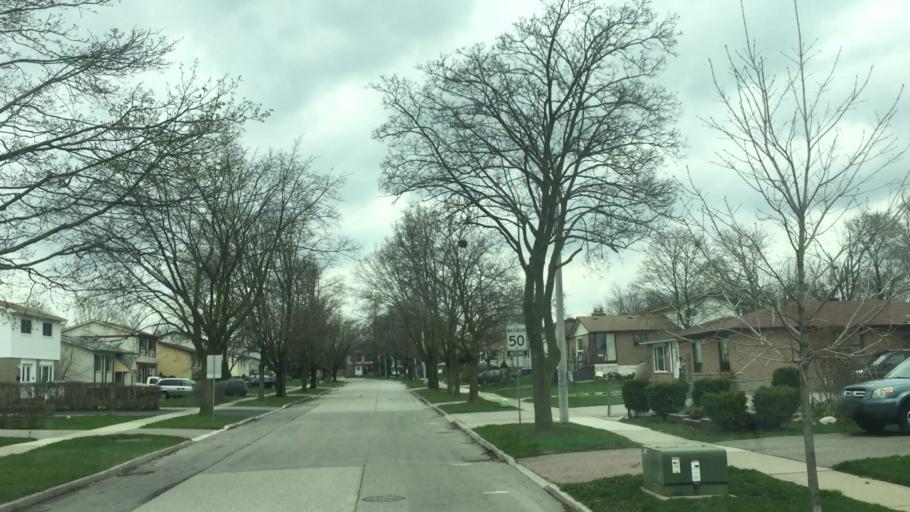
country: CA
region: Ontario
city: Brampton
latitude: 43.7059
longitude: -79.7482
